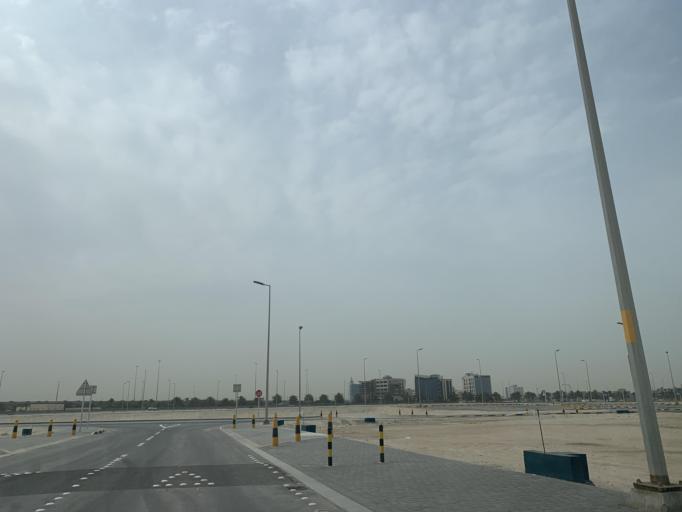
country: BH
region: Northern
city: Madinat `Isa
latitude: 26.1838
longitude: 50.5081
